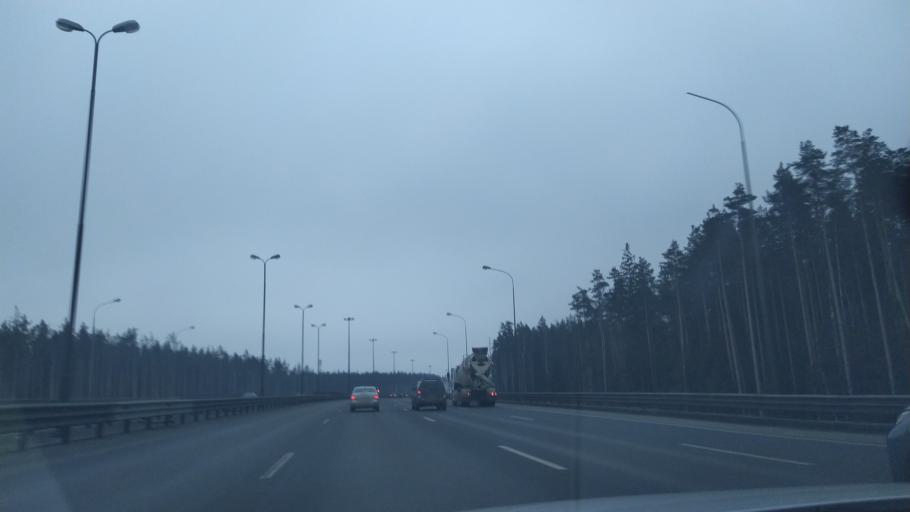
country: RU
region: Leningrad
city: Yanino Vtoroye
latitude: 59.9658
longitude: 30.5531
